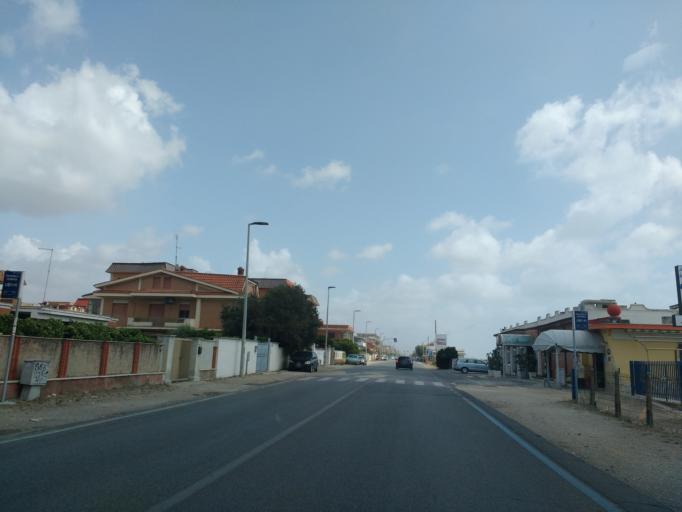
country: IT
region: Latium
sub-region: Citta metropolitana di Roma Capitale
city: Torvaianica Alta
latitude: 41.6086
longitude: 12.4758
